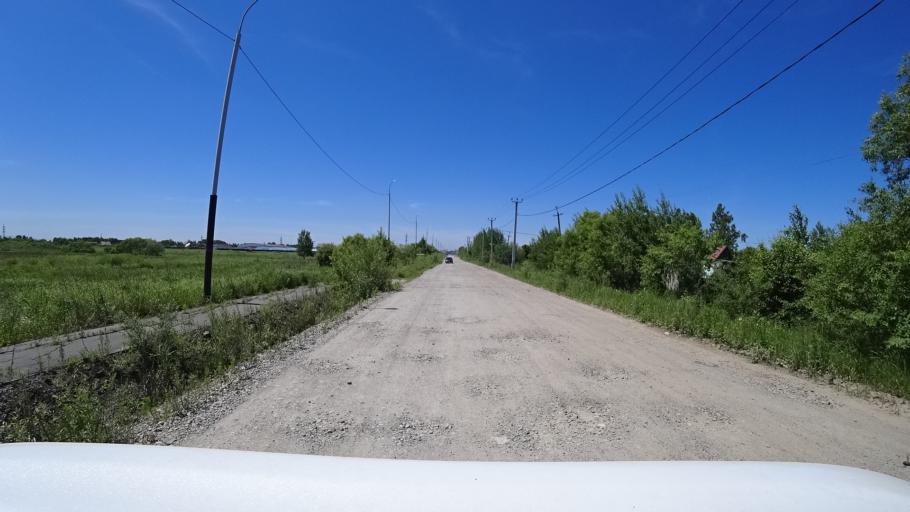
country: RU
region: Khabarovsk Krai
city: Topolevo
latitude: 48.5010
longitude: 135.1912
